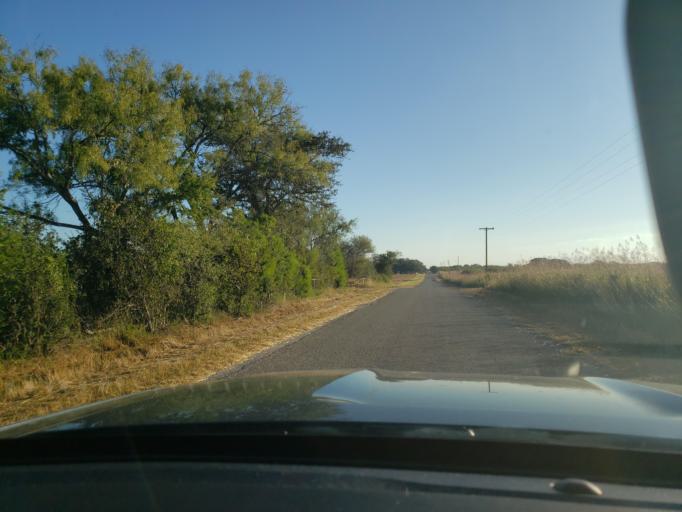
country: US
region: Texas
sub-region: Bee County
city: Beeville
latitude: 28.4193
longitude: -97.7148
